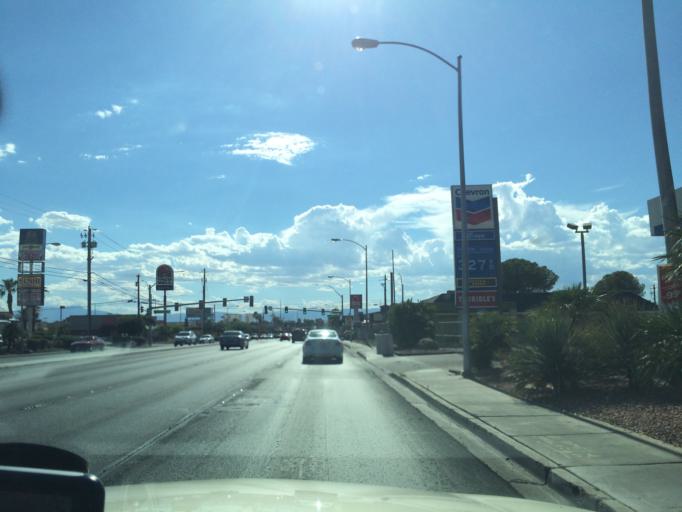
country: US
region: Nevada
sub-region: Clark County
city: Winchester
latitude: 36.1001
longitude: -115.1133
